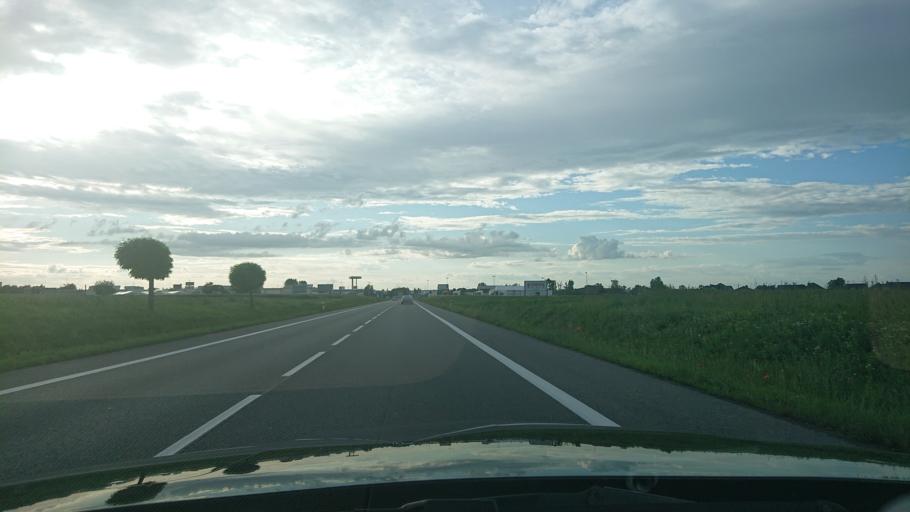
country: PL
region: Greater Poland Voivodeship
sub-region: Powiat gnieznienski
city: Gniezno
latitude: 52.5591
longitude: 17.6187
